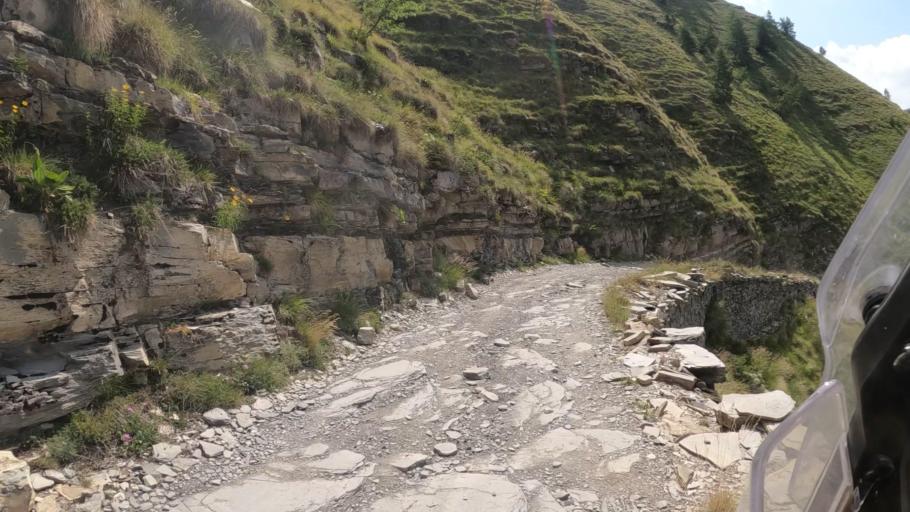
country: IT
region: Piedmont
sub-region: Provincia di Cuneo
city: Briga Alta
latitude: 44.0739
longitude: 7.7103
